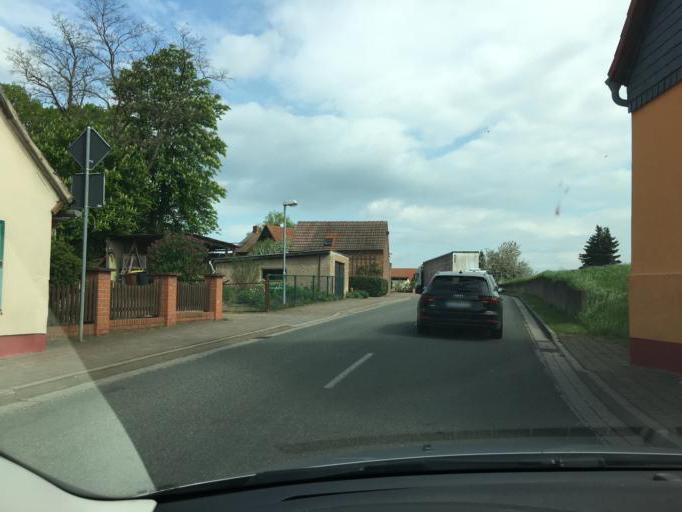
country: DE
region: Saxony-Anhalt
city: Grobzig
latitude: 51.6610
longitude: 11.8404
